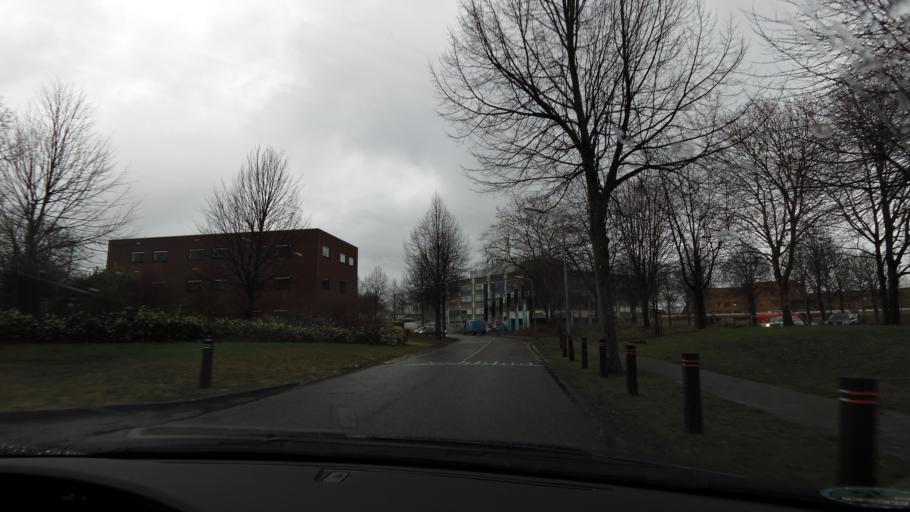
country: NL
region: Limburg
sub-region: Gemeente Sittard-Geleen
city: Sittard
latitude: 51.0021
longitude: 5.8561
